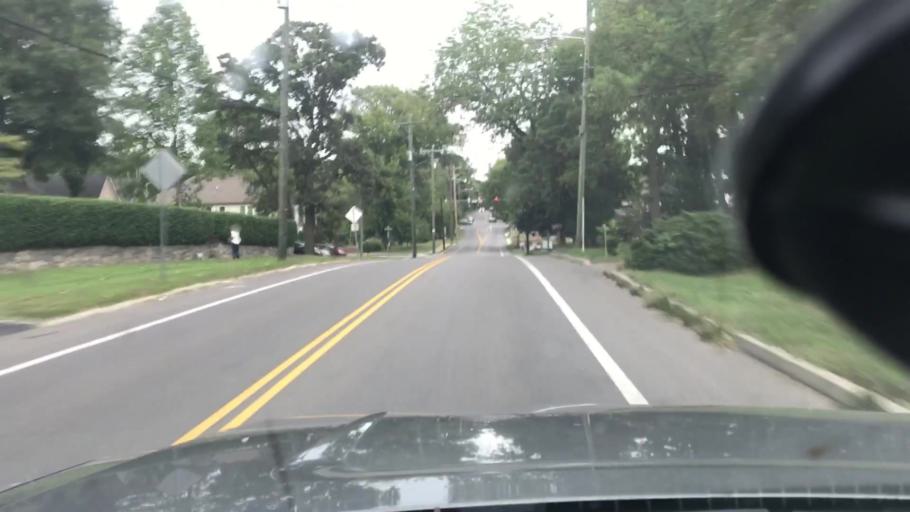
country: US
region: Tennessee
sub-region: Davidson County
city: Belle Meade
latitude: 36.1167
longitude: -86.8389
